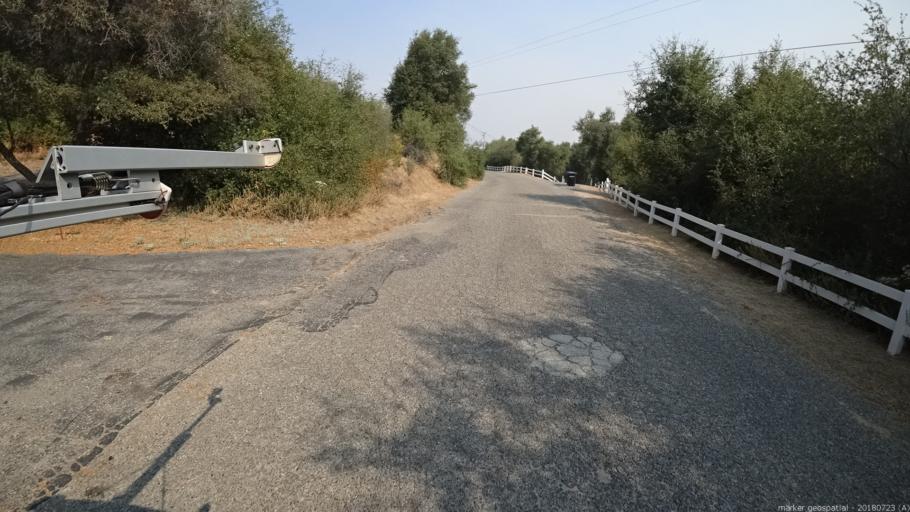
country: US
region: California
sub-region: Madera County
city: Ahwahnee
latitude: 37.3489
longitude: -119.6967
